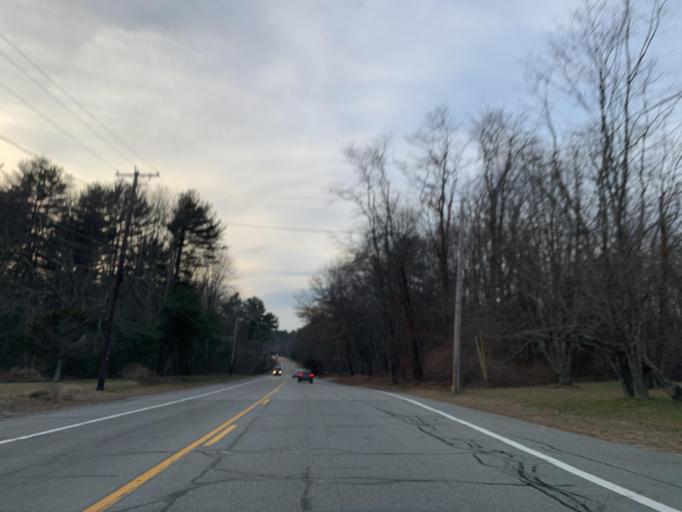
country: US
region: Rhode Island
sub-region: Providence County
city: Chepachet
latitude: 41.9193
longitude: -71.6891
